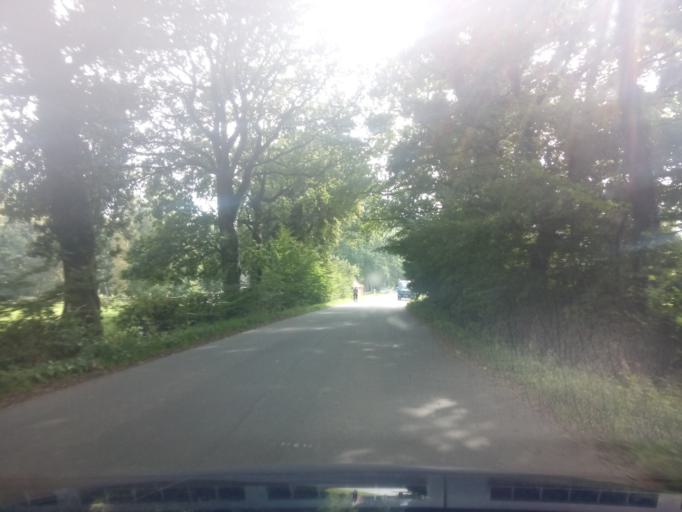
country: DE
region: Lower Saxony
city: Osterholz-Scharmbeck
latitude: 53.2397
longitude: 8.7633
